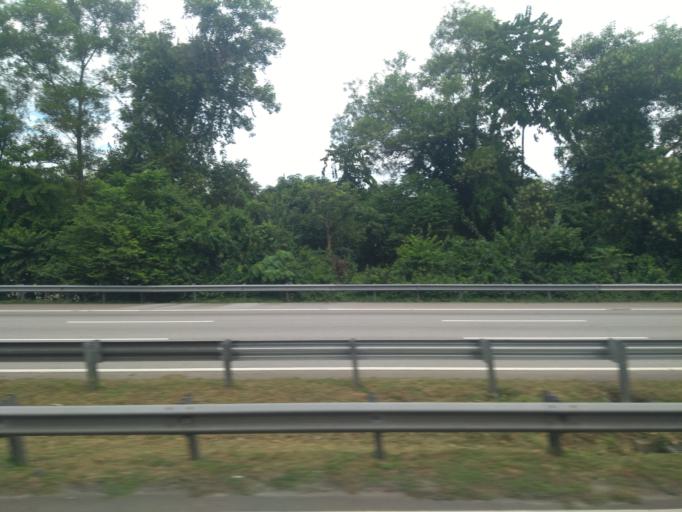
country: MY
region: Melaka
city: Pulau Sebang
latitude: 2.4434
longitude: 102.1950
